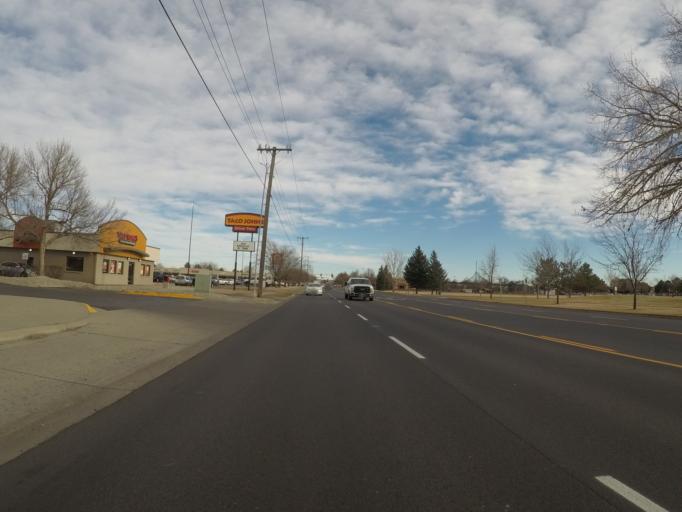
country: US
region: Montana
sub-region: Yellowstone County
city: Billings
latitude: 45.7698
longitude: -108.5842
